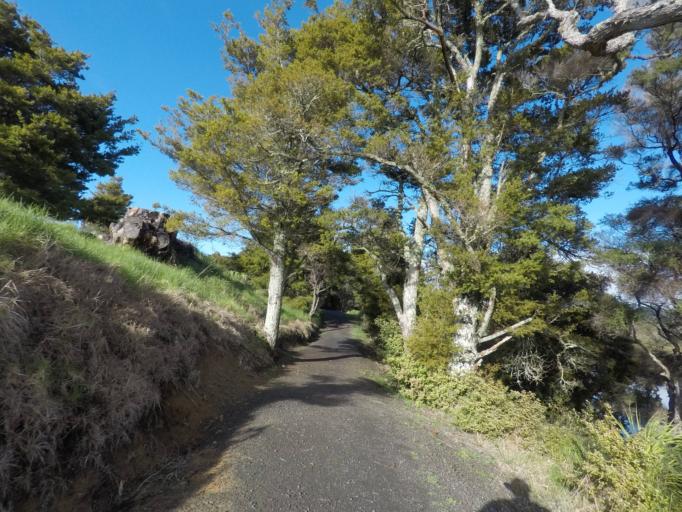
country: NZ
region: Auckland
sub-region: Auckland
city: Warkworth
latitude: -36.4275
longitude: 174.7184
